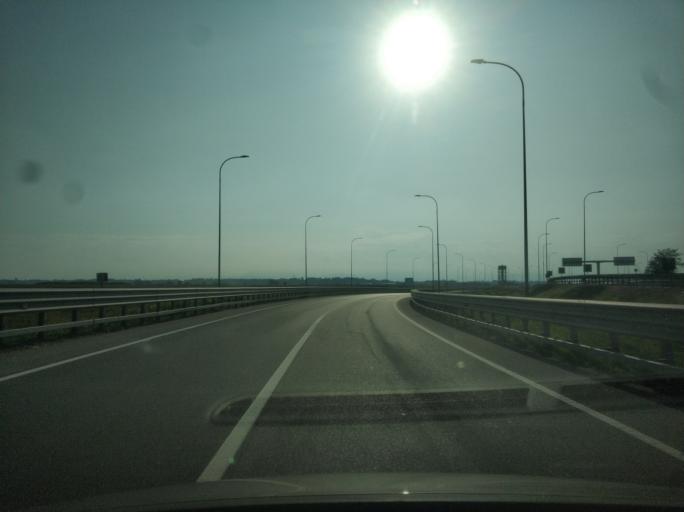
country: IT
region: Piedmont
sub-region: Provincia di Cuneo
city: Roreto
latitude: 44.6629
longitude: 7.8086
